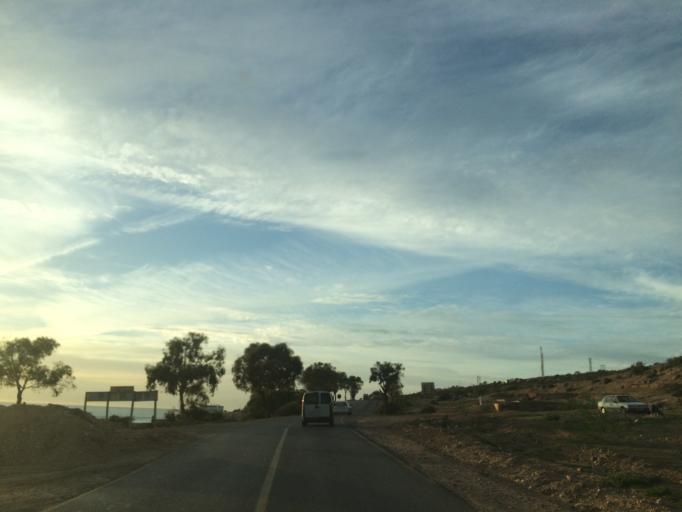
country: MA
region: Souss-Massa-Draa
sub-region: Agadir-Ida-ou-Tnan
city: Taghazout
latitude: 30.5427
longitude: -9.7019
